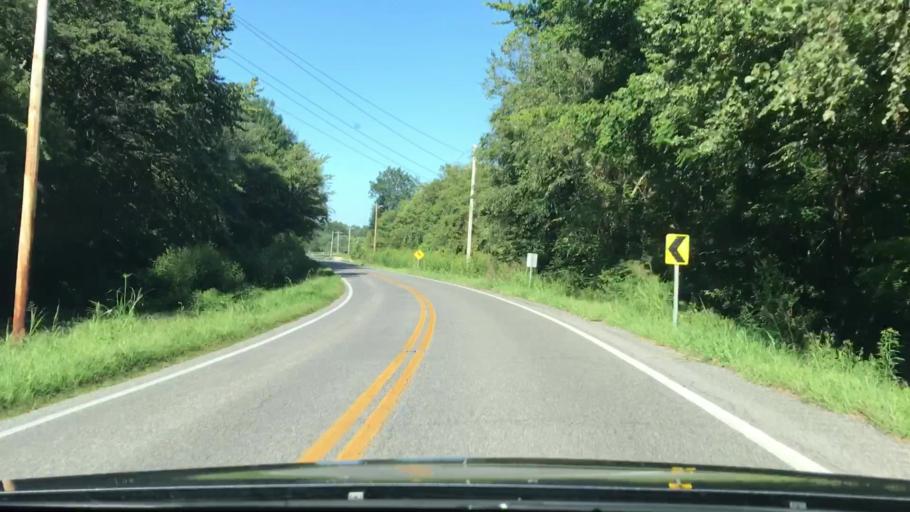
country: US
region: Kentucky
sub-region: Graves County
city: Mayfield
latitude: 36.7821
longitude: -88.5271
